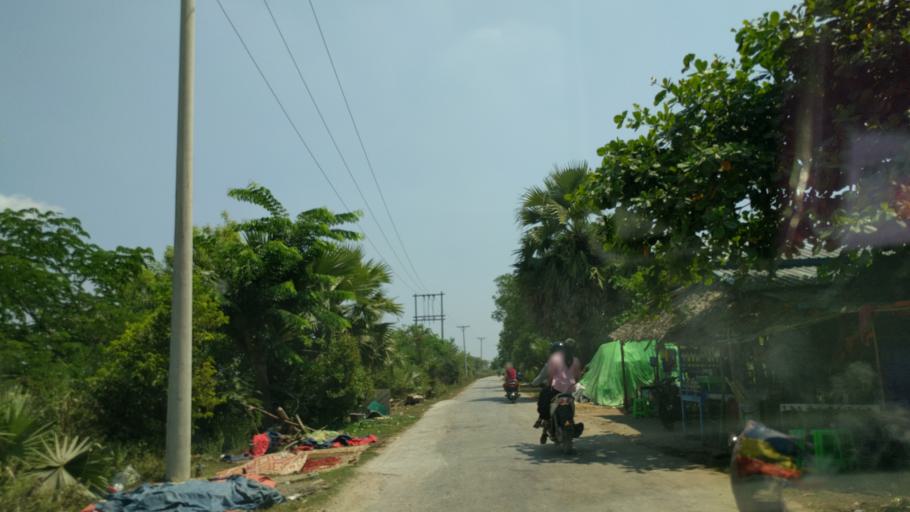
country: MM
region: Mon
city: Martaban
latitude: 16.5855
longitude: 97.6618
